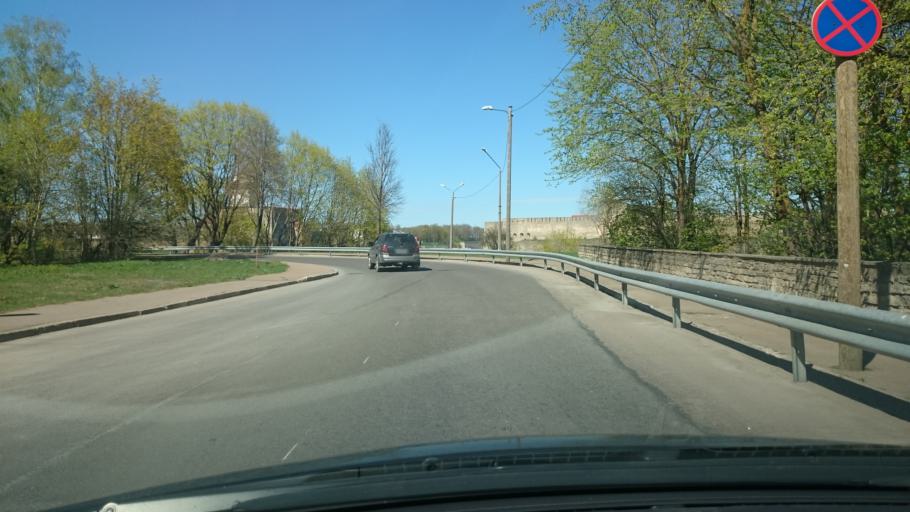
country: RU
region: Leningrad
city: Ivangorod
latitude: 59.3710
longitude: 28.2037
